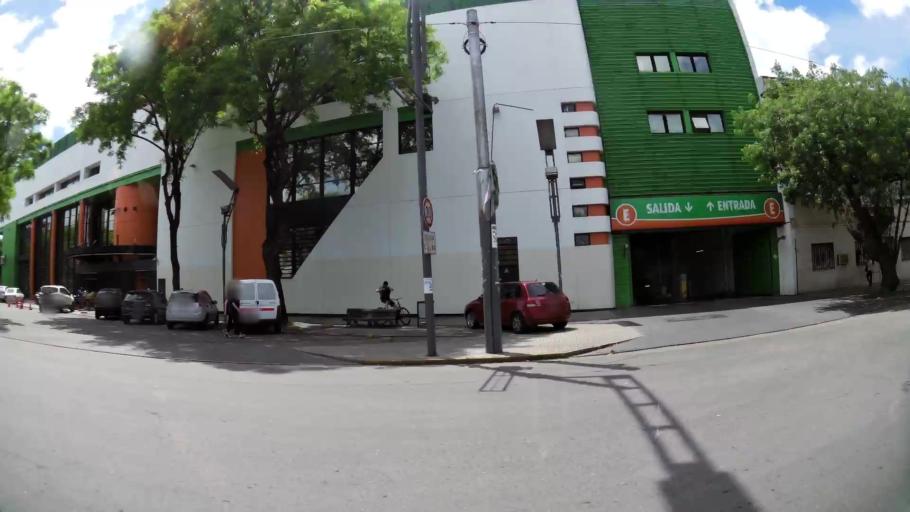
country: AR
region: Santa Fe
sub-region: Departamento de Rosario
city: Rosario
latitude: -32.9780
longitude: -60.6441
